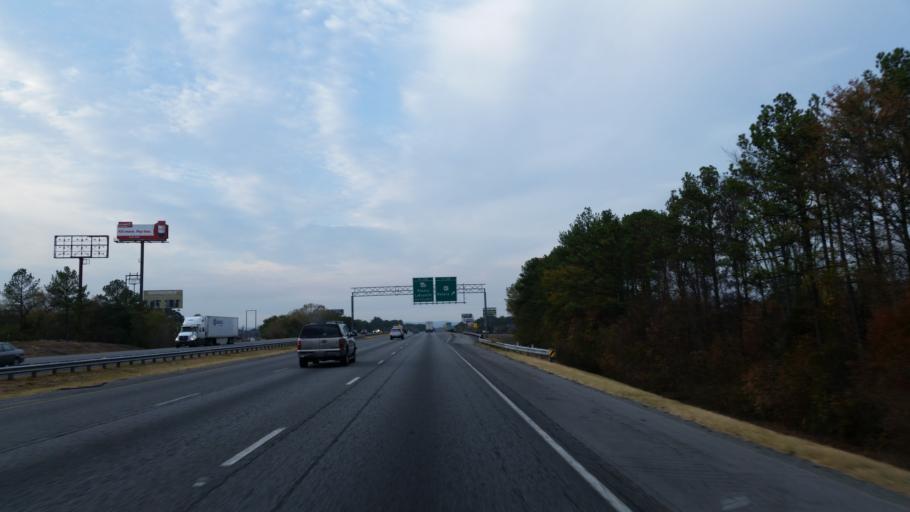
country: US
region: Georgia
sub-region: Gordon County
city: Calhoun
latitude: 34.5538
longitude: -84.9328
